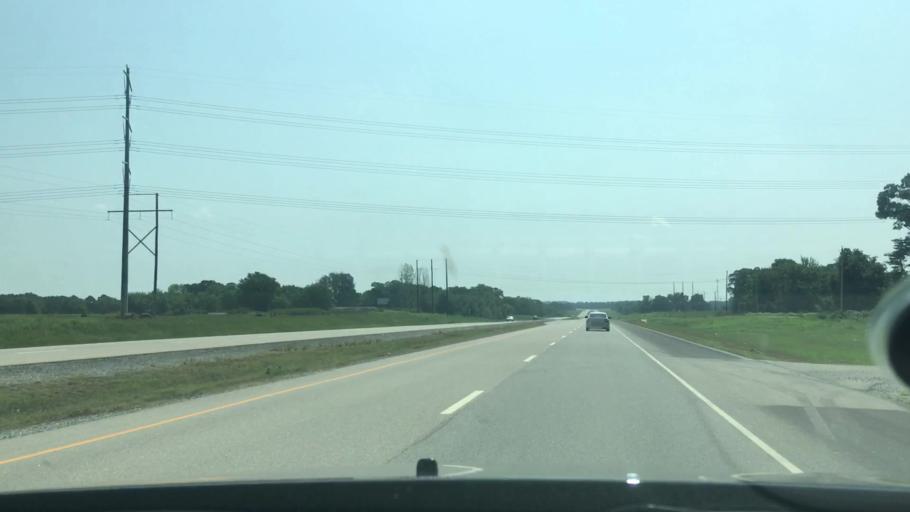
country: US
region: Oklahoma
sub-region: Atoka County
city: Atoka
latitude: 34.3323
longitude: -96.0523
